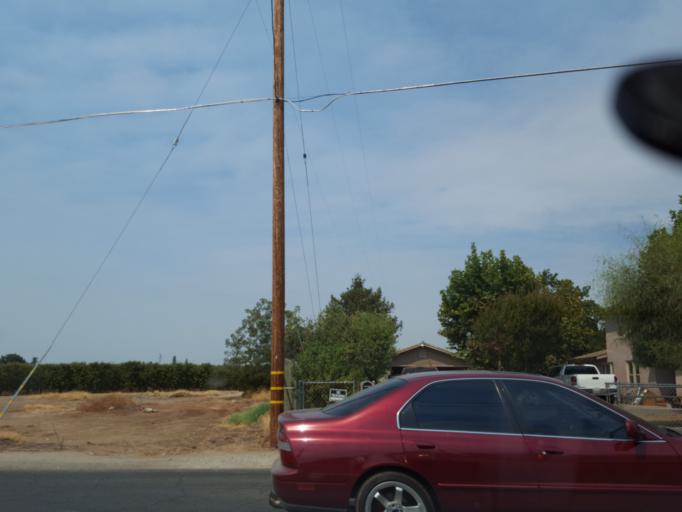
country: US
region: California
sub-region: Fresno County
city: Reedley
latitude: 36.6114
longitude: -119.4398
